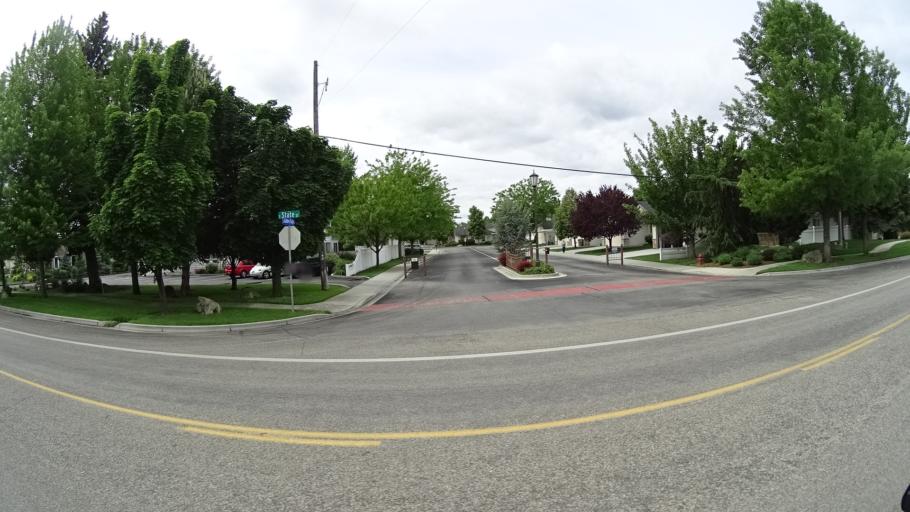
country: US
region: Idaho
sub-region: Ada County
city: Eagle
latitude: 43.6923
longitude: -116.3380
